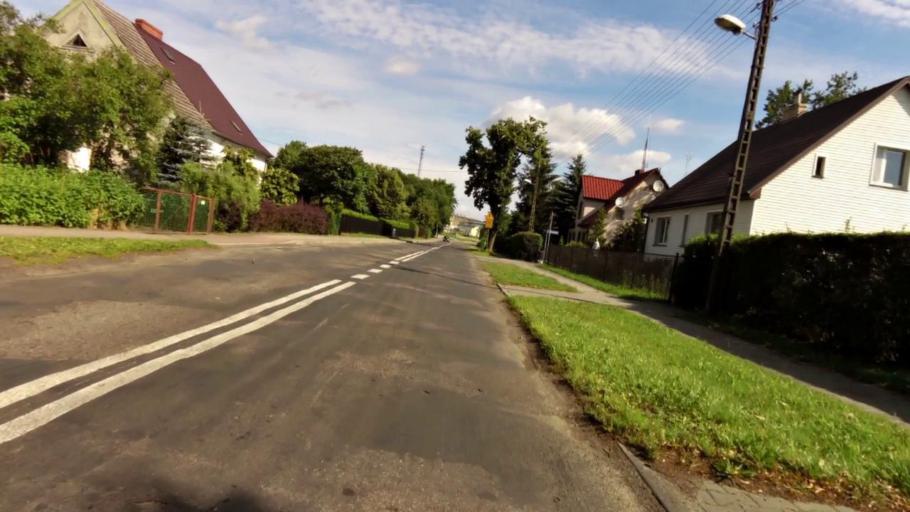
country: PL
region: West Pomeranian Voivodeship
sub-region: Powiat stargardzki
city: Dobrzany
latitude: 53.3635
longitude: 15.4283
